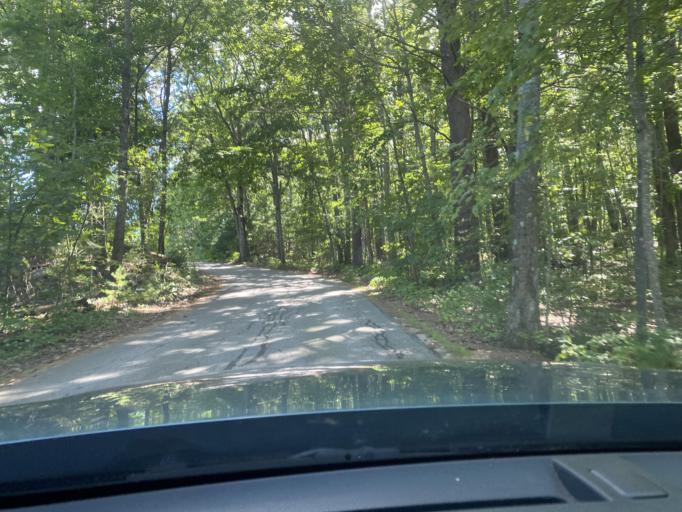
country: US
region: New Hampshire
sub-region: Rockingham County
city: Portsmouth
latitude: 43.0546
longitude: -70.7561
